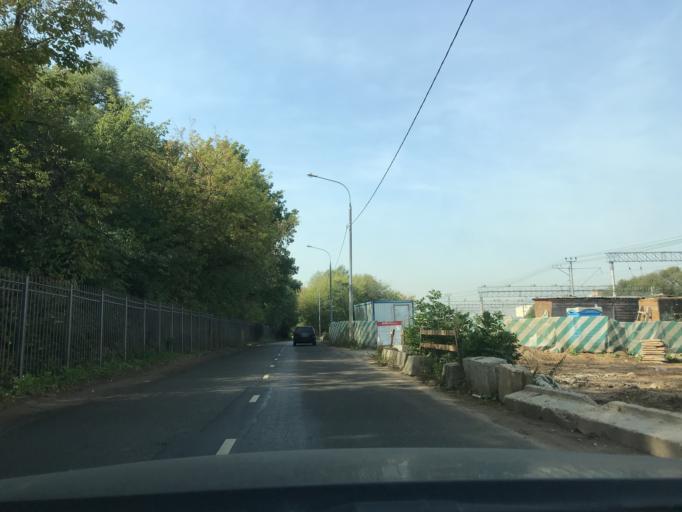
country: RU
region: Moscow
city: Perovo
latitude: 55.7371
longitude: 37.7843
